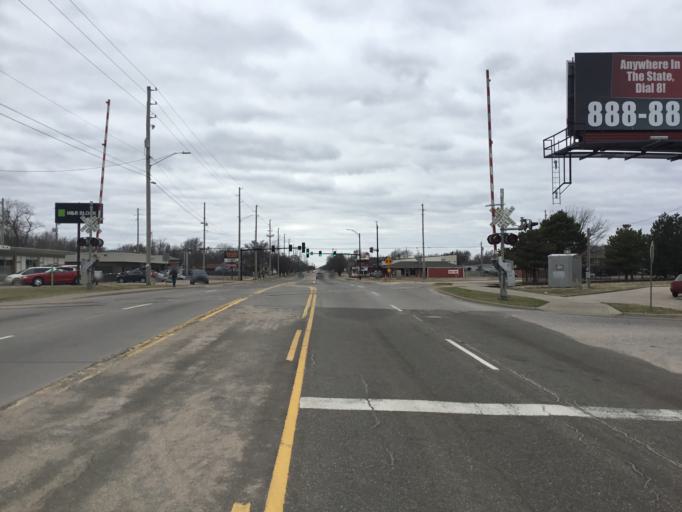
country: US
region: Kansas
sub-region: Sedgwick County
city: Wichita
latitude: 37.6949
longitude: -97.3789
